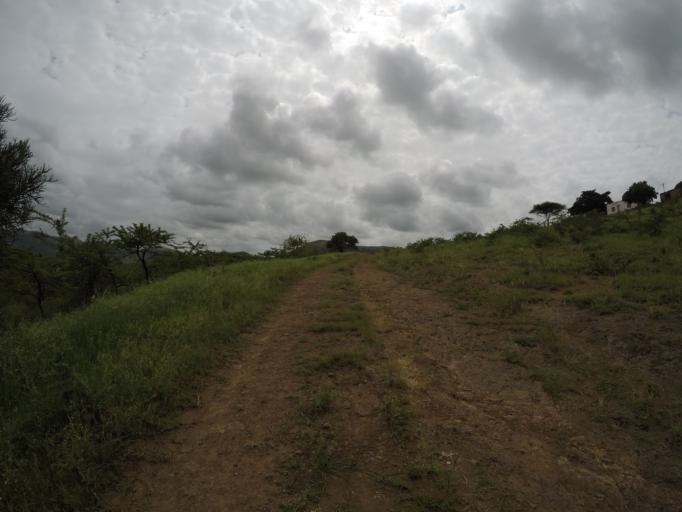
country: ZA
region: KwaZulu-Natal
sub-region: uThungulu District Municipality
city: Empangeni
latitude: -28.6163
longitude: 31.8877
